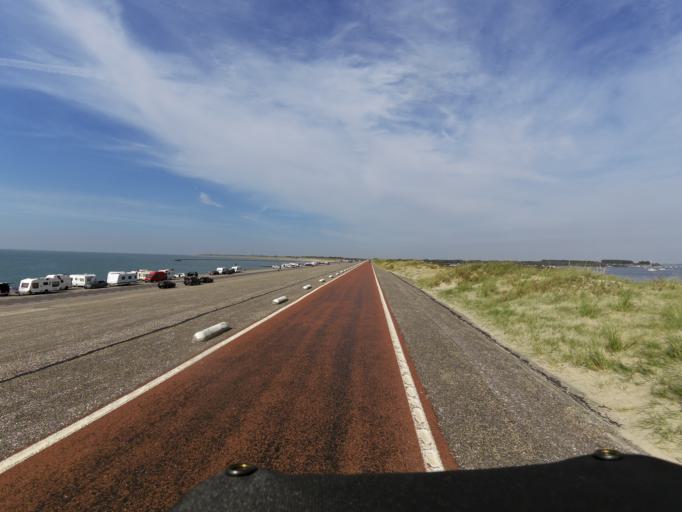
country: NL
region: Zeeland
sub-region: Schouwen-Duiveland
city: Scharendijke
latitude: 51.7725
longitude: 3.8622
